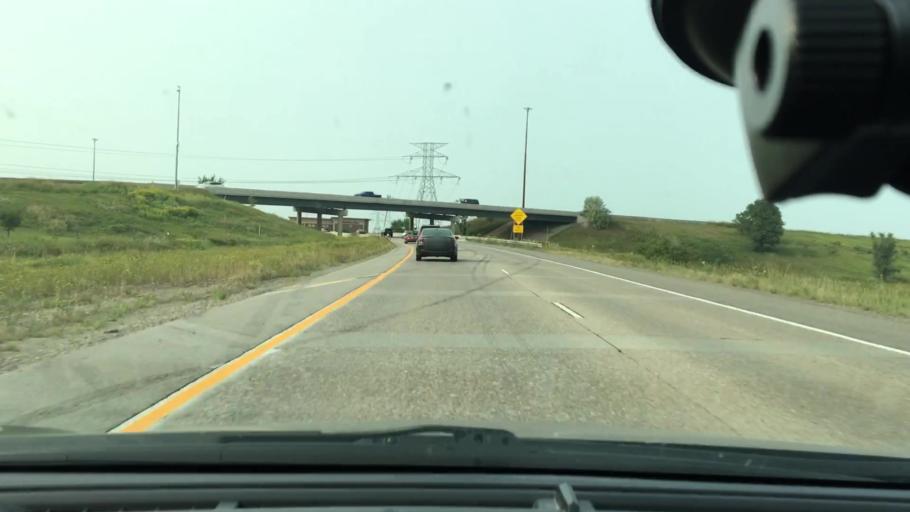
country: US
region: Minnesota
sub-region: Hennepin County
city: Maple Grove
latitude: 45.0901
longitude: -93.4462
